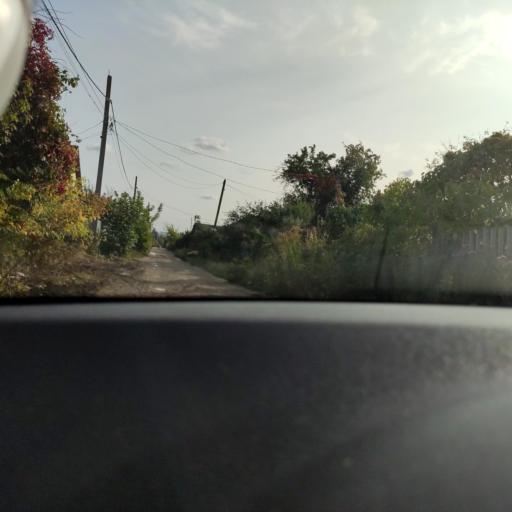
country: RU
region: Samara
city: Petra-Dubrava
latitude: 53.2827
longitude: 50.2953
